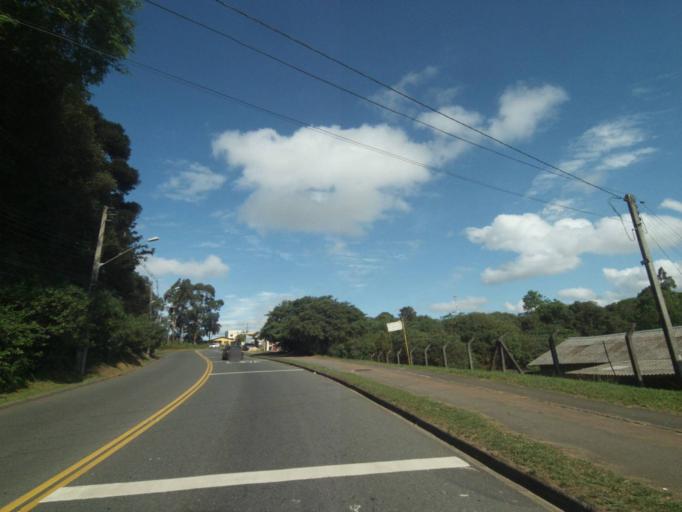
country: BR
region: Parana
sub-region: Curitiba
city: Curitiba
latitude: -25.3883
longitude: -49.3003
